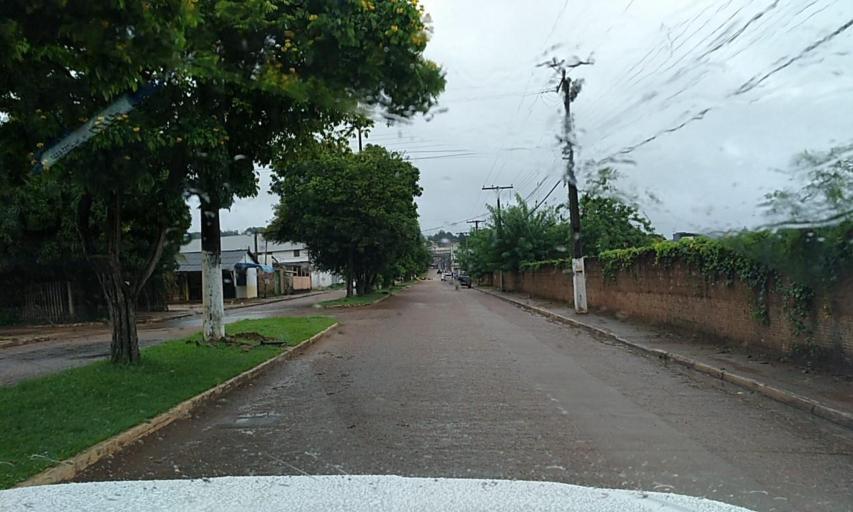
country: BR
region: Para
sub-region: Altamira
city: Altamira
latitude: -3.2123
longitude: -52.2229
